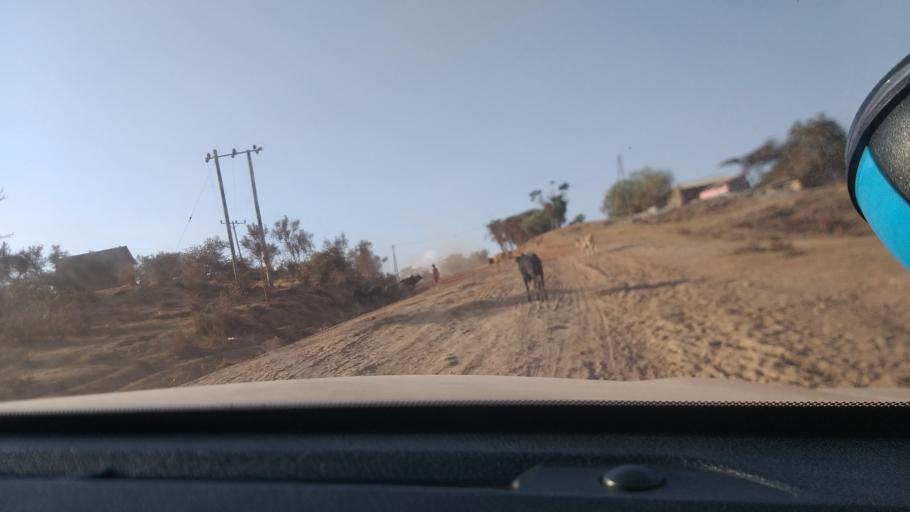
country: ET
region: Oromiya
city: Shashemene
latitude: 7.4877
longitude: 38.7233
